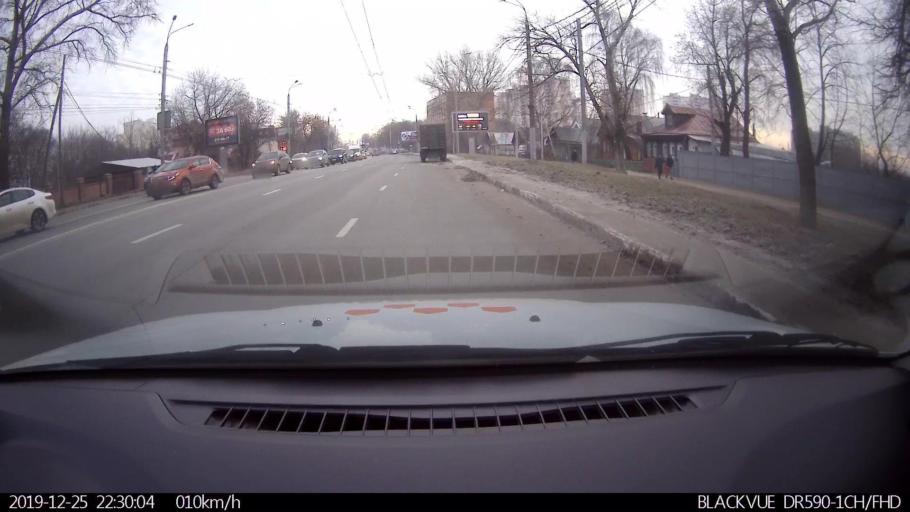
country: RU
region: Nizjnij Novgorod
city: Bor
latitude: 56.3203
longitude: 44.0560
